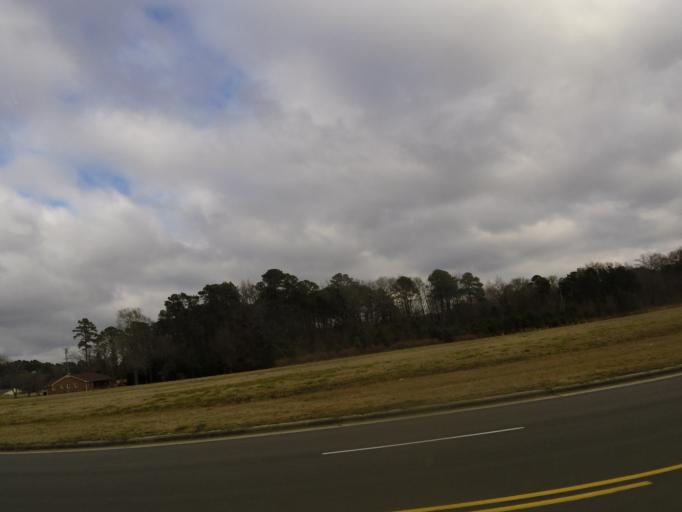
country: US
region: North Carolina
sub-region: Nash County
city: Rocky Mount
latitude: 35.9447
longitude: -77.8495
